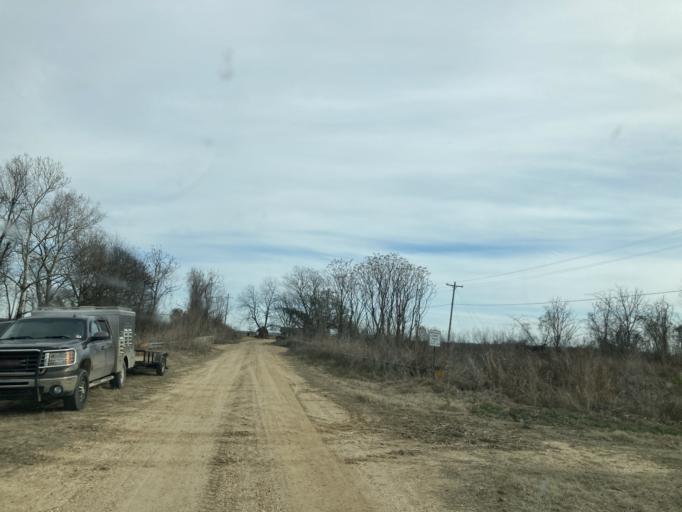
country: US
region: Mississippi
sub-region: Humphreys County
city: Belzoni
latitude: 33.1527
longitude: -90.6083
